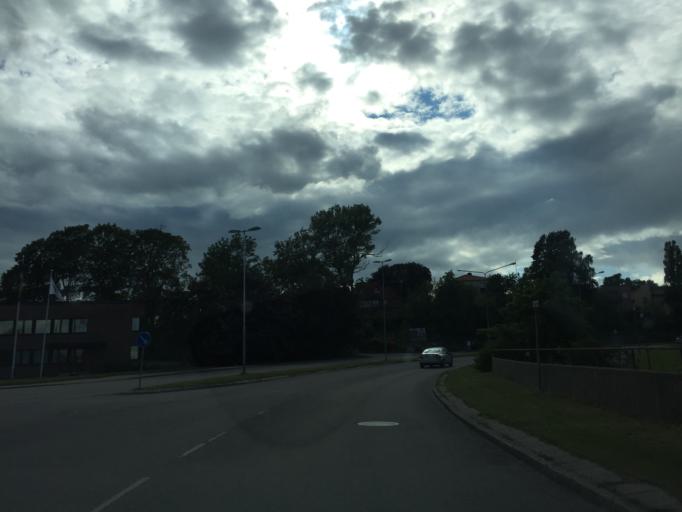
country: SE
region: Vaestmanland
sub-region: Vasteras
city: Vasteras
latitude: 59.6058
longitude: 16.5450
